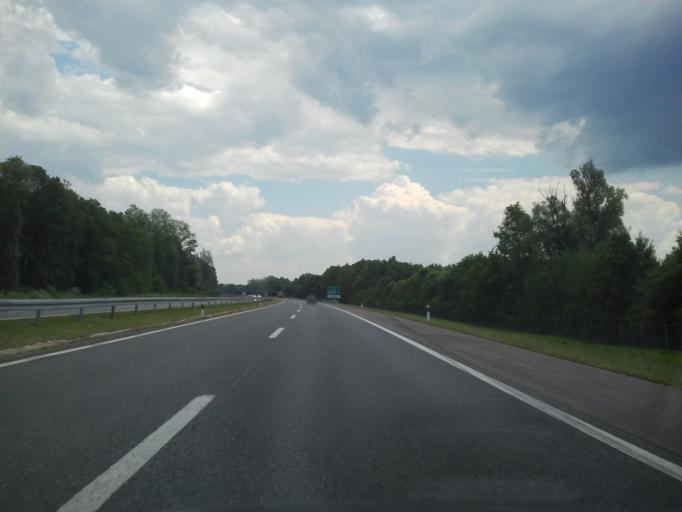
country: HR
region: Sisacko-Moslavacka
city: Novska
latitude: 45.3122
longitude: 16.9899
